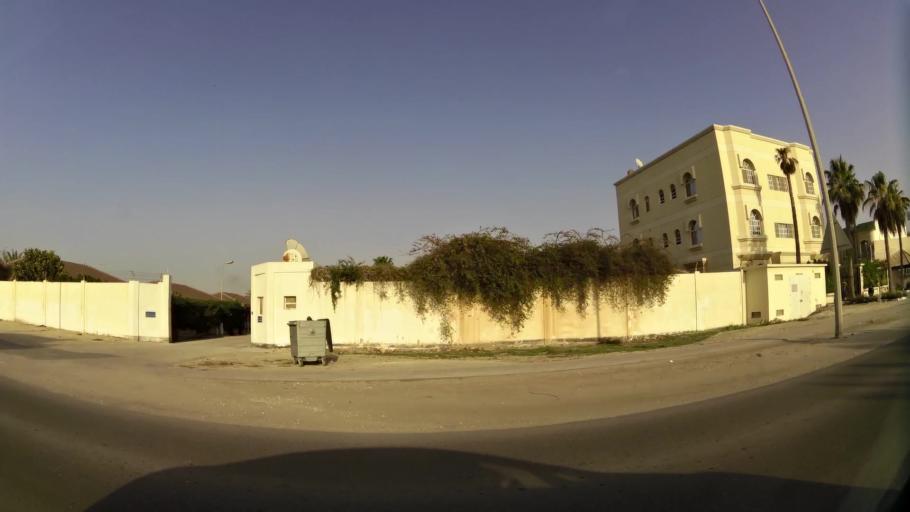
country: BH
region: Manama
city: Jidd Hafs
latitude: 26.2118
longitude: 50.4805
